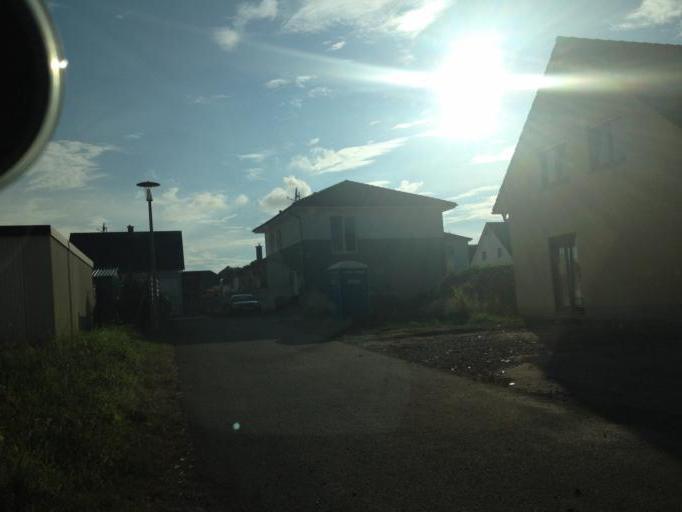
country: DE
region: Saarland
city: Neunkirchen
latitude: 49.3660
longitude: 7.1653
